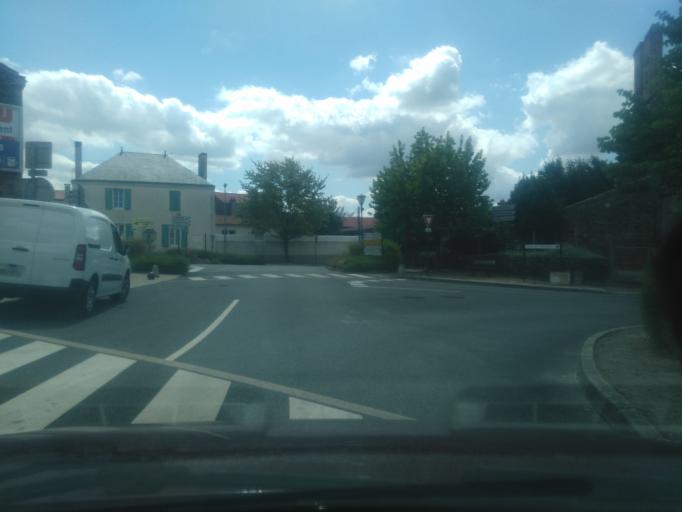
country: FR
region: Pays de la Loire
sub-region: Departement de la Vendee
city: Chauche
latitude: 46.8291
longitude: -1.2728
